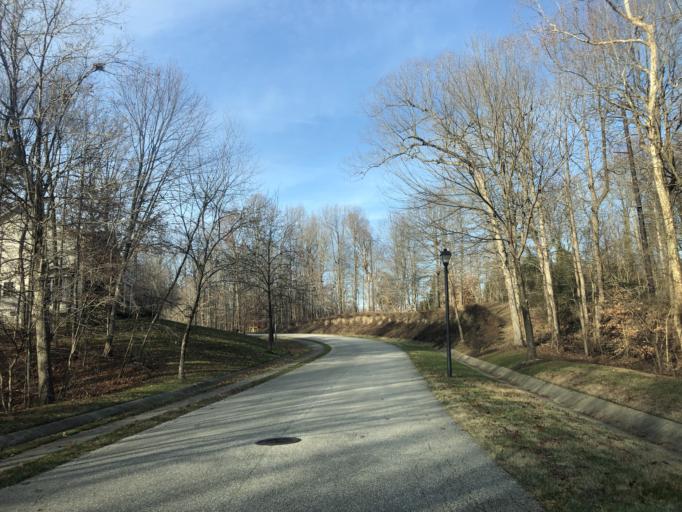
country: US
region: Maryland
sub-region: Anne Arundel County
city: Crownsville
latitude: 39.0367
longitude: -76.6052
